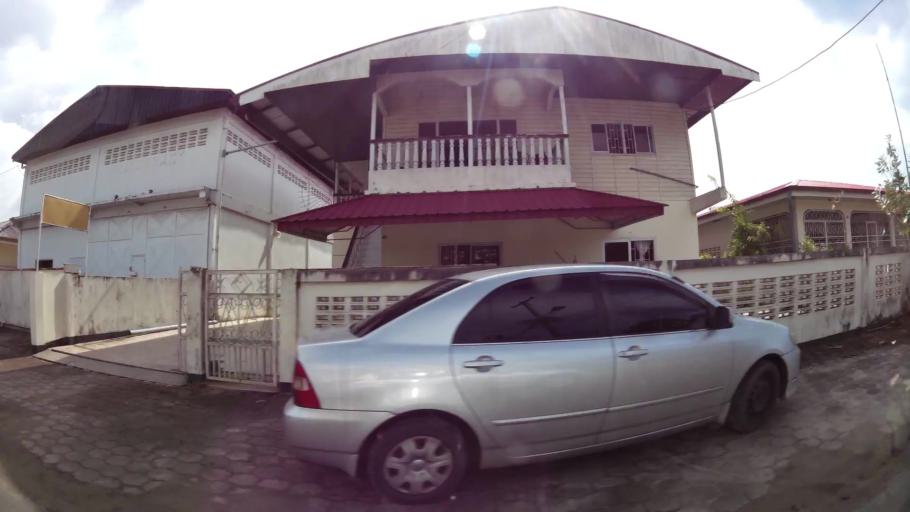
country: SR
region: Paramaribo
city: Paramaribo
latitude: 5.8475
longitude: -55.2082
